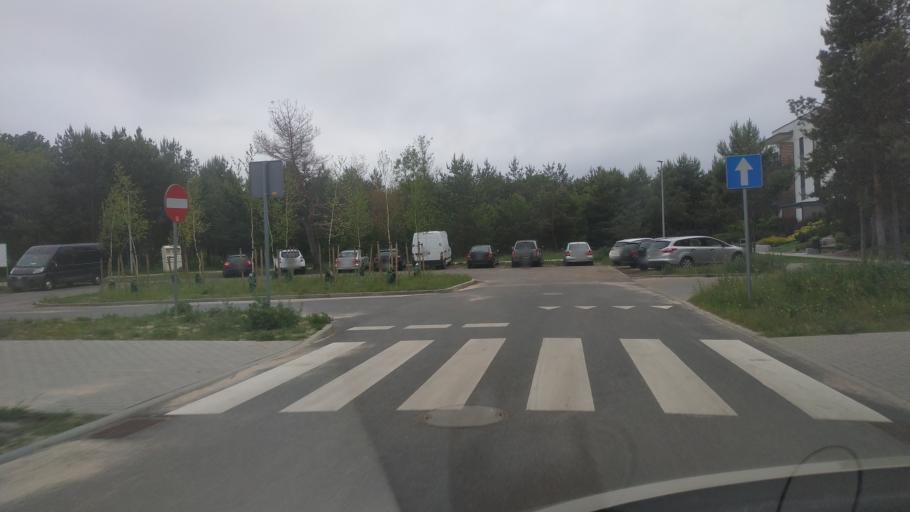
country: PL
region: Kujawsko-Pomorskie
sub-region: Torun
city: Torun
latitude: 53.0454
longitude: 18.6059
